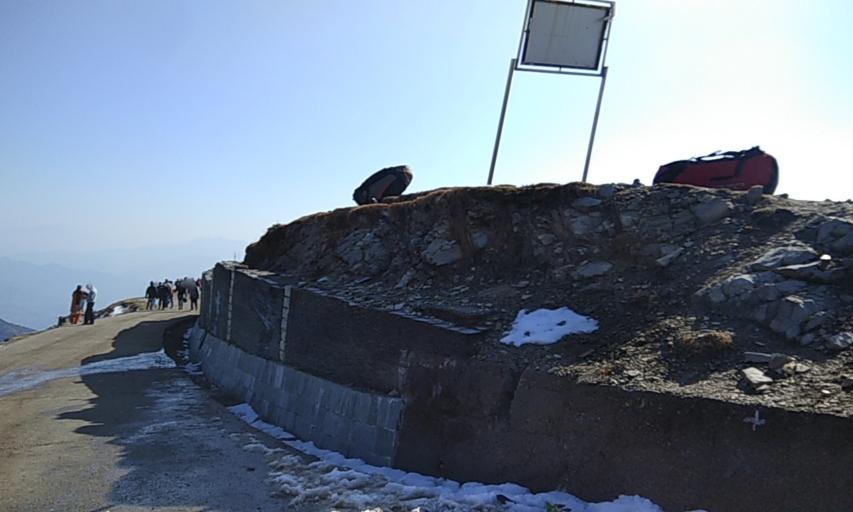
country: IN
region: Himachal Pradesh
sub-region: Mandi
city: Jogindarnagar
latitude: 32.0585
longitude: 76.7441
